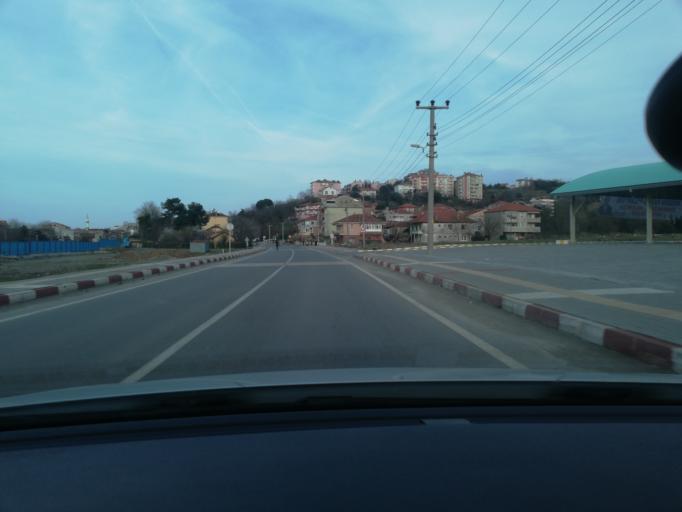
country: TR
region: Zonguldak
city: Tieum
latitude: 41.5579
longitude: 32.0174
